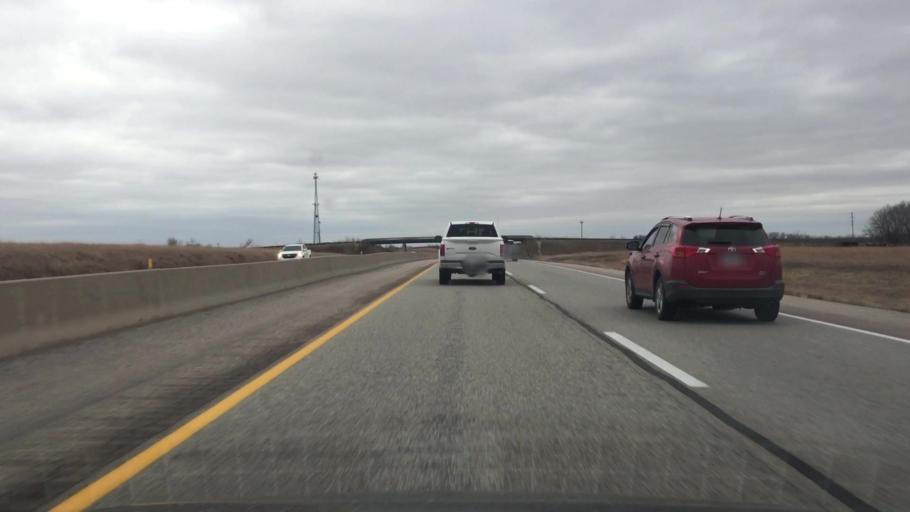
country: US
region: Kansas
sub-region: Butler County
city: El Dorado
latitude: 37.9637
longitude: -96.7290
